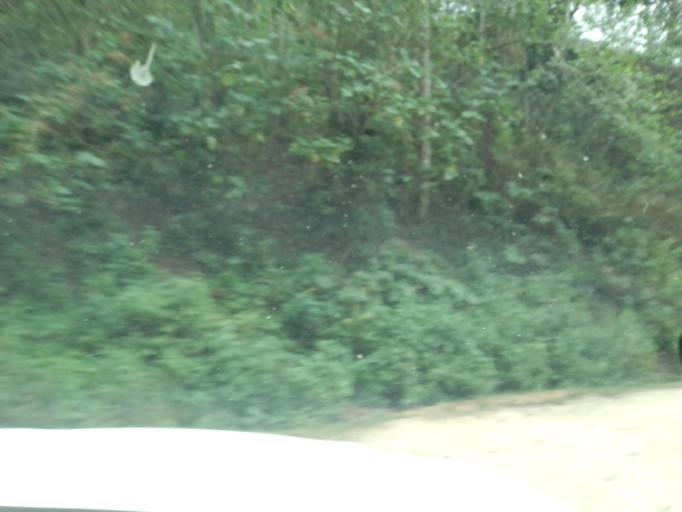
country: MX
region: Chiapas
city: Motozintla de Mendoza
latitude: 15.2208
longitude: -92.2268
